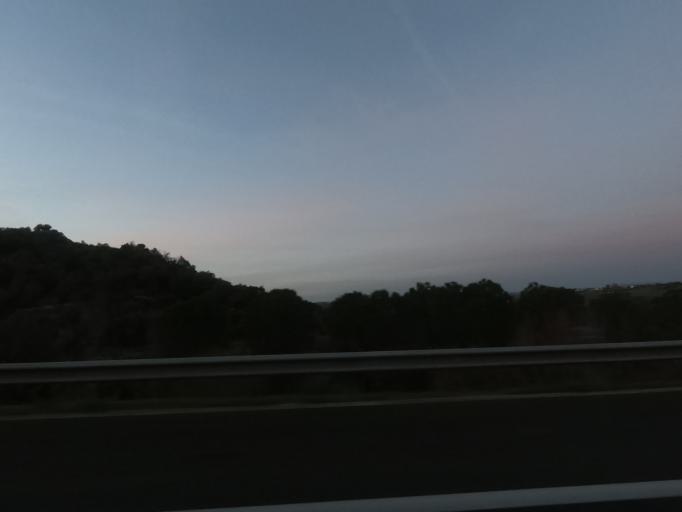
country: PT
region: Santarem
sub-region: Santarem
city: Santarem
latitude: 39.2410
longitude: -8.7486
